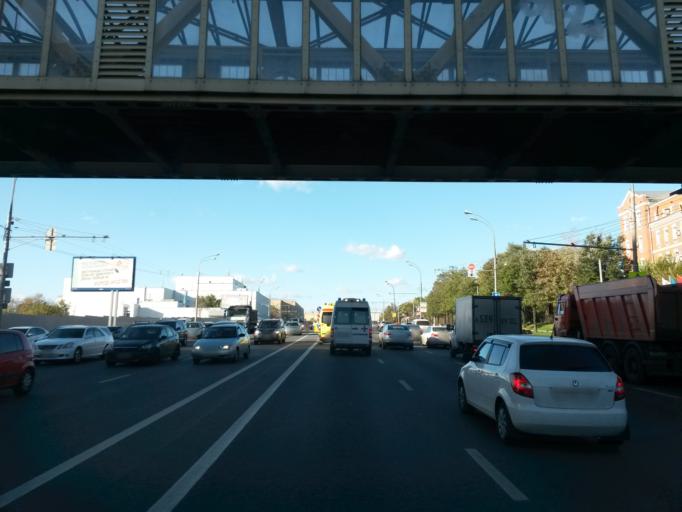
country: RU
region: Moscow
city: Novyye Cheremushki
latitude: 55.6940
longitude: 37.6213
